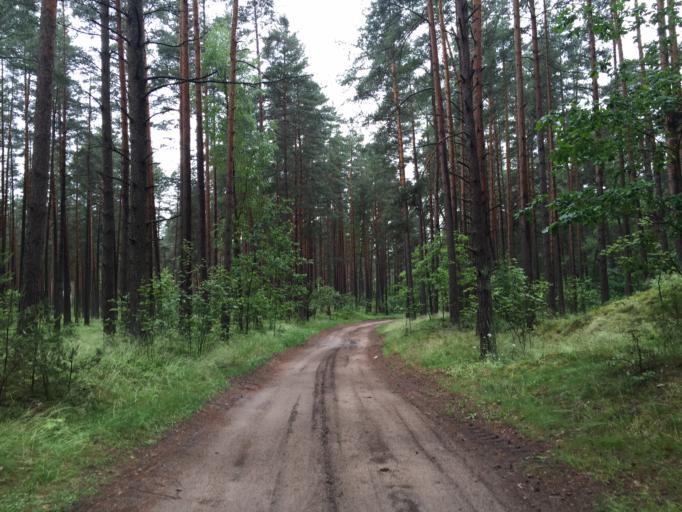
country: LV
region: Riga
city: Jaunciems
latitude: 57.0720
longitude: 24.1469
